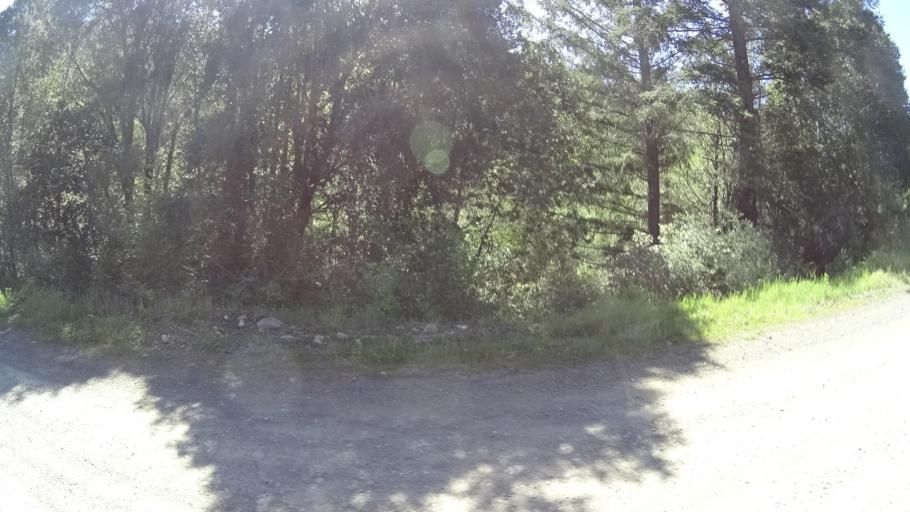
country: US
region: California
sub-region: Humboldt County
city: Rio Dell
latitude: 40.2266
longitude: -124.1100
